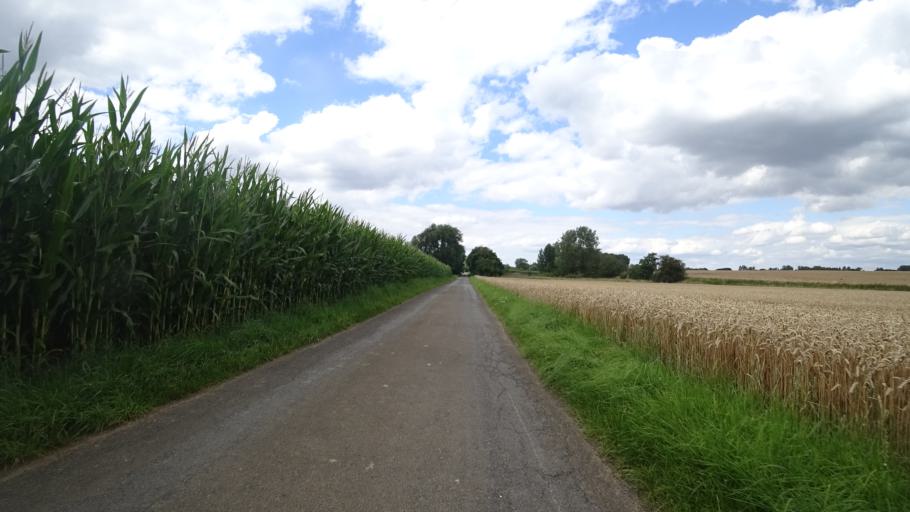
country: DE
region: North Rhine-Westphalia
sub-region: Regierungsbezirk Detmold
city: Petershagen
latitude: 52.4033
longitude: 8.9924
